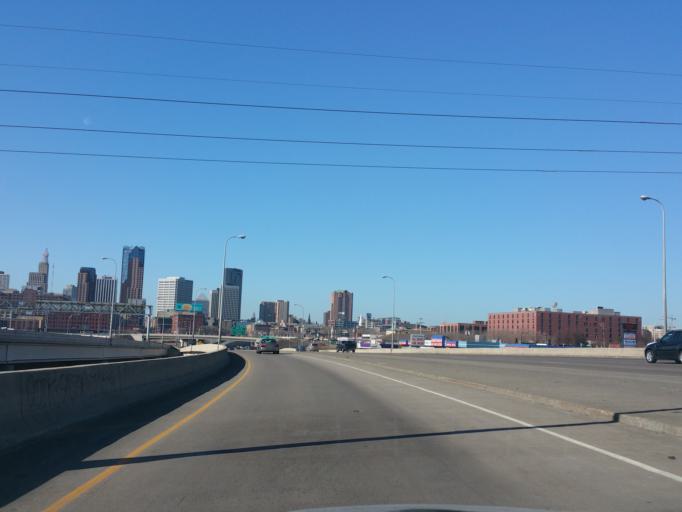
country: US
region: Minnesota
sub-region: Ramsey County
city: Saint Paul
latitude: 44.9549
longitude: -93.0778
